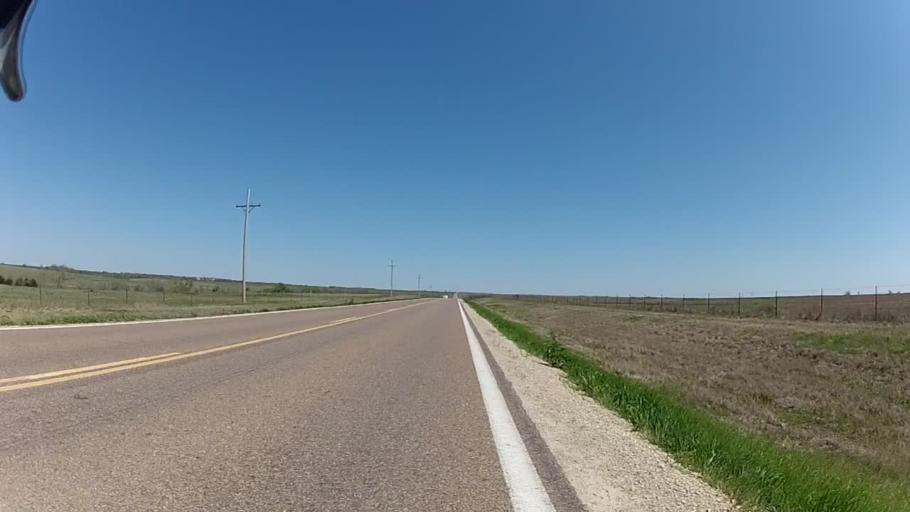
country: US
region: Kansas
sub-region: Morris County
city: Council Grove
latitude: 38.9001
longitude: -96.5202
